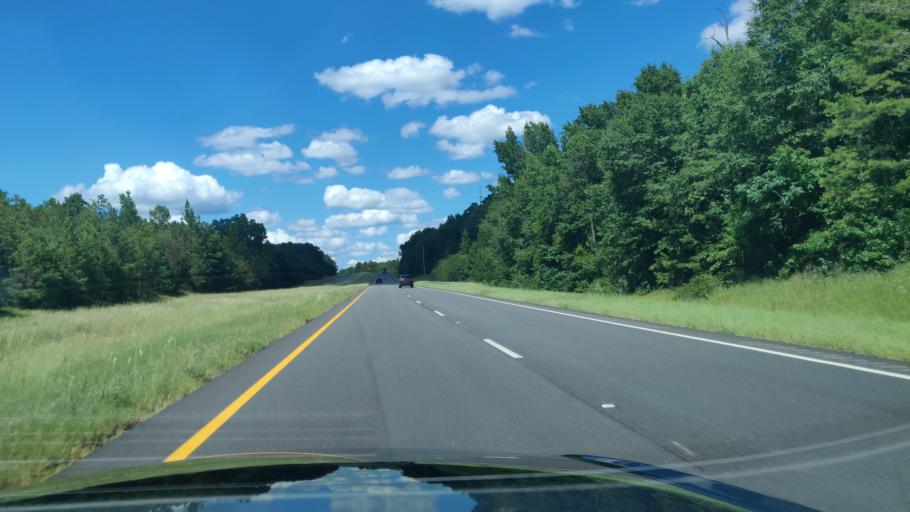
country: US
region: Georgia
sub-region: Stewart County
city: Richland
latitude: 32.0943
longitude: -84.6748
